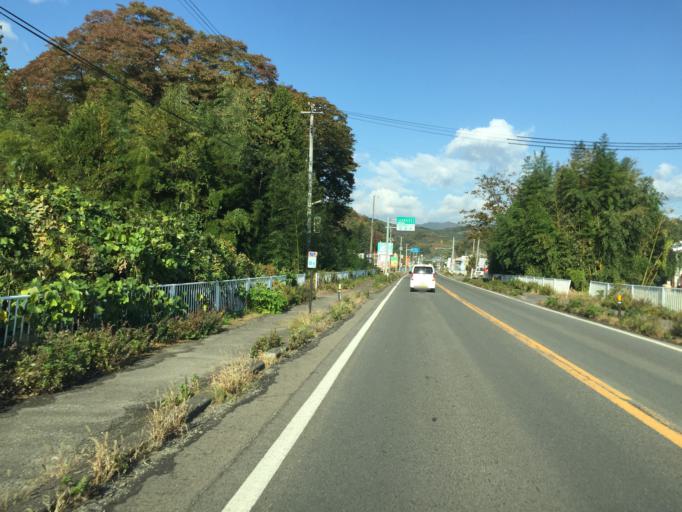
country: JP
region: Fukushima
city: Fukushima-shi
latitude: 37.8199
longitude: 140.4344
